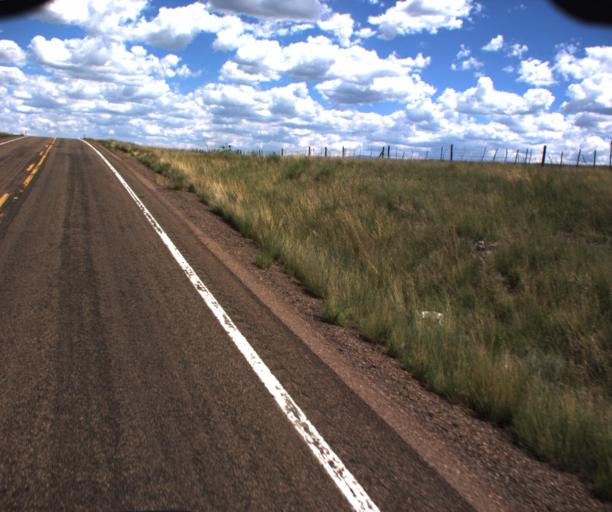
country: US
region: Arizona
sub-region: Apache County
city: Springerville
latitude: 34.1989
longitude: -109.3931
